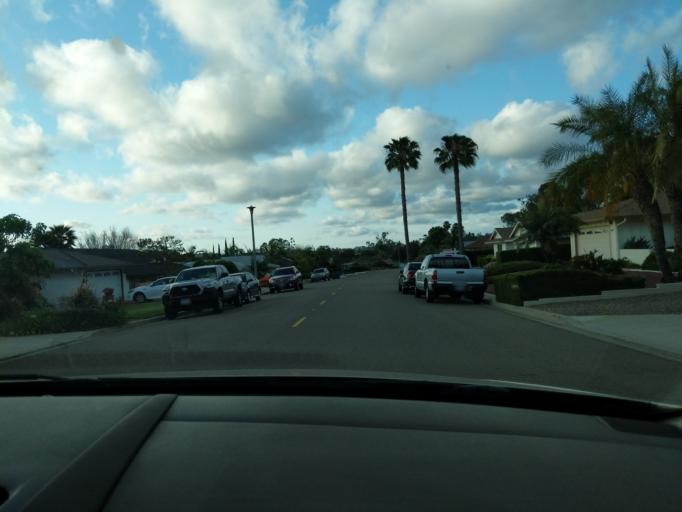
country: US
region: California
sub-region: San Diego County
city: Lake San Marcos
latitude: 33.1212
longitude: -117.2001
